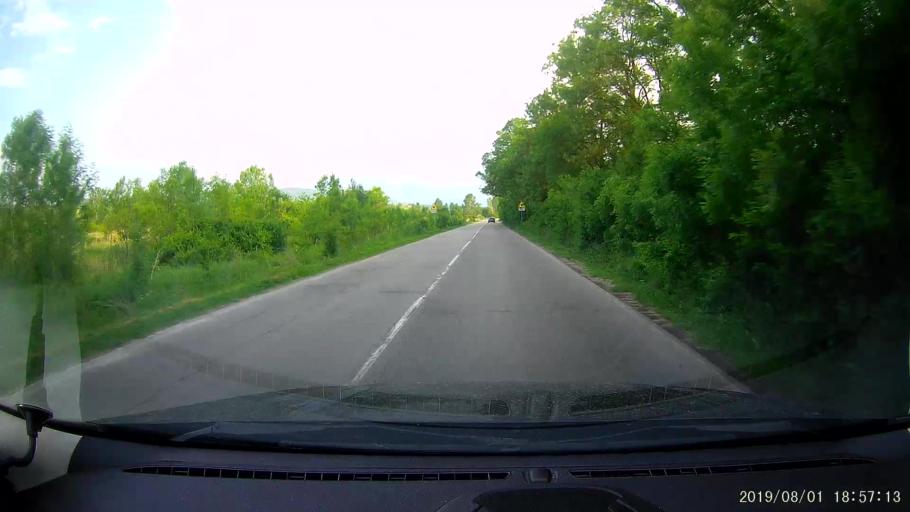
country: BG
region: Shumen
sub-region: Obshtina Smyadovo
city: Smyadovo
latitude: 43.1509
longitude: 27.0216
